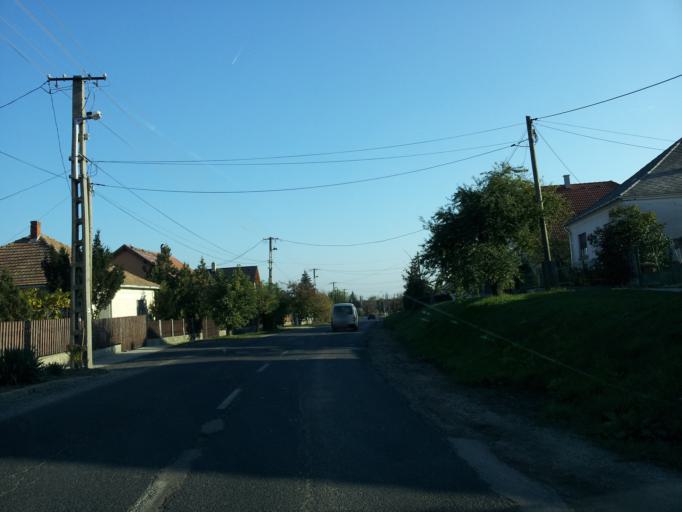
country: HU
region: Fejer
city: Bodajk
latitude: 47.3178
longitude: 18.2466
